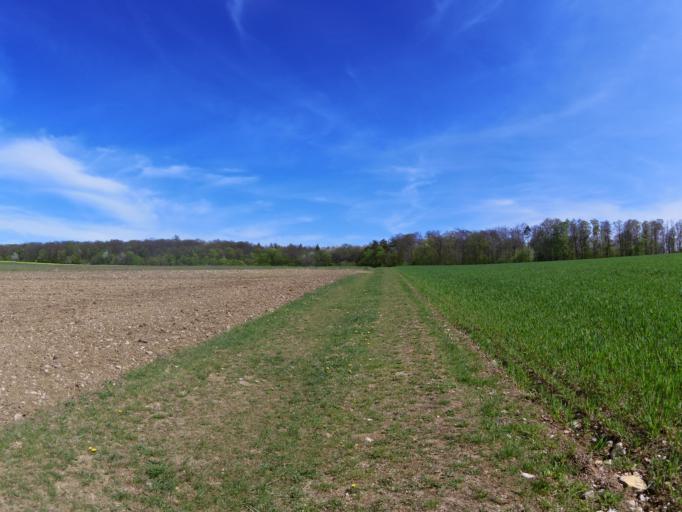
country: DE
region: Bavaria
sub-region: Regierungsbezirk Unterfranken
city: Rimpar
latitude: 49.8623
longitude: 9.9754
